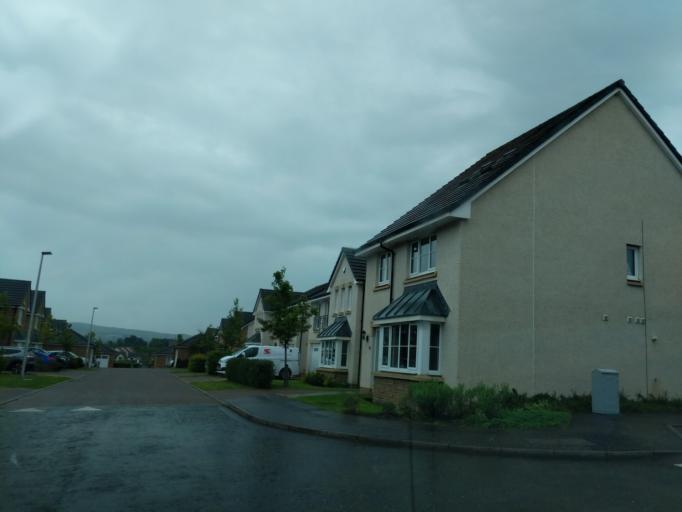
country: GB
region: Scotland
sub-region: Midlothian
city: Bonnyrigg
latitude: 55.8689
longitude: -3.1003
